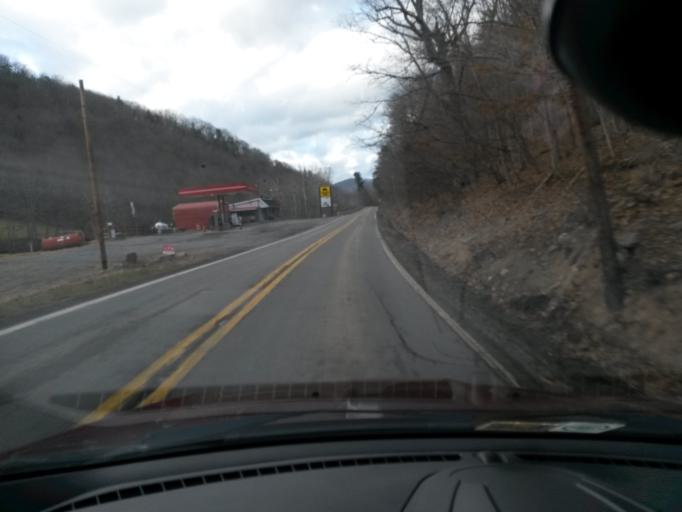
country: US
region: West Virginia
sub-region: Monroe County
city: Union
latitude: 37.5112
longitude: -80.6116
